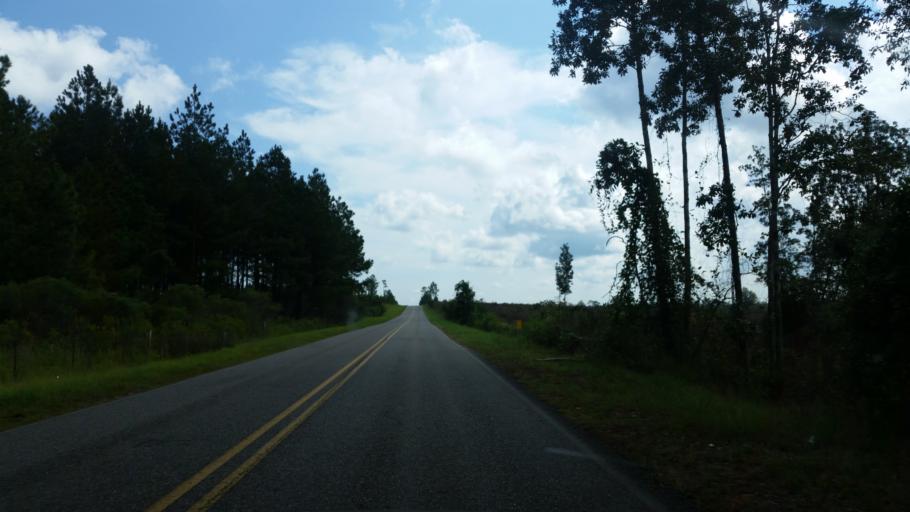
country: US
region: Florida
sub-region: Escambia County
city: Cantonment
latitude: 30.6885
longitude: -87.4506
